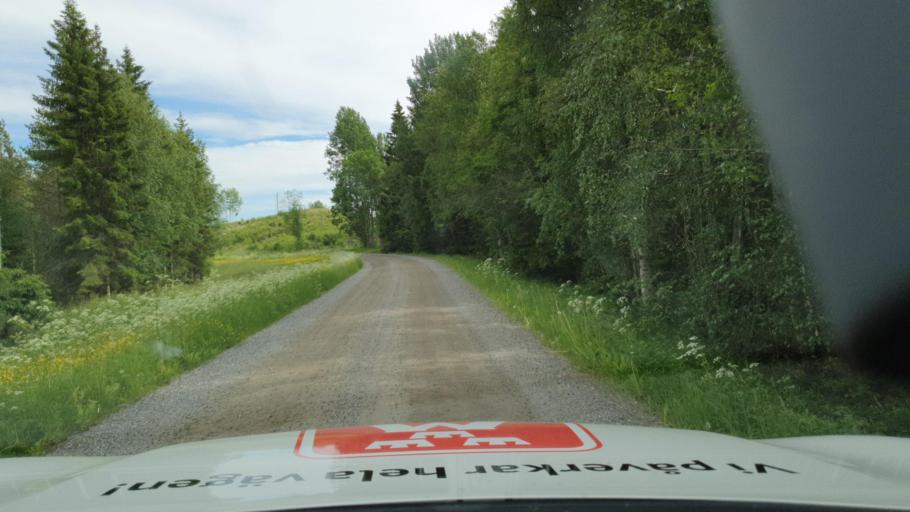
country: SE
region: Vaesterbotten
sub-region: Robertsfors Kommun
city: Robertsfors
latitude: 64.3922
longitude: 21.0224
